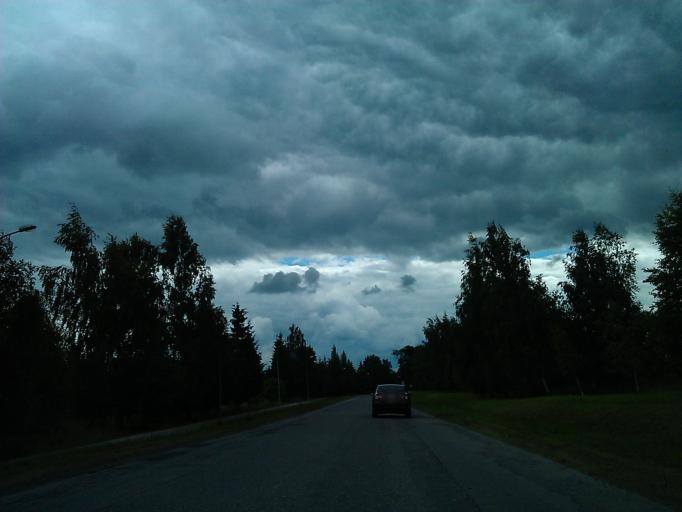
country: LV
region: Dobeles Rajons
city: Dobele
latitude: 56.6294
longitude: 23.2650
